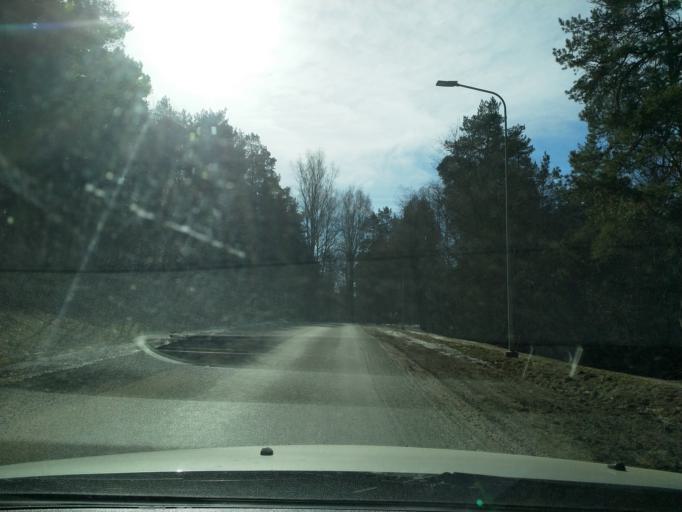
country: LV
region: Valmieras Rajons
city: Valmiera
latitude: 57.5267
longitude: 25.4211
